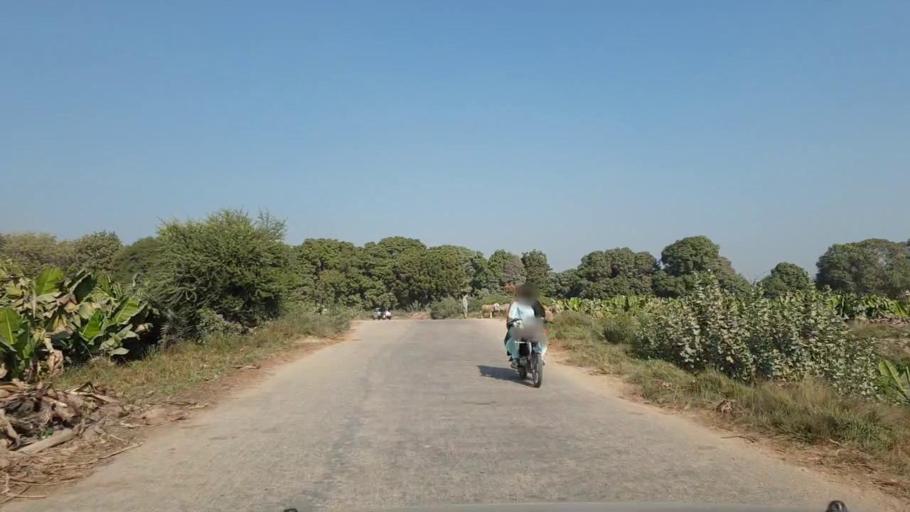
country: PK
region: Sindh
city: Matiari
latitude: 25.6185
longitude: 68.5942
